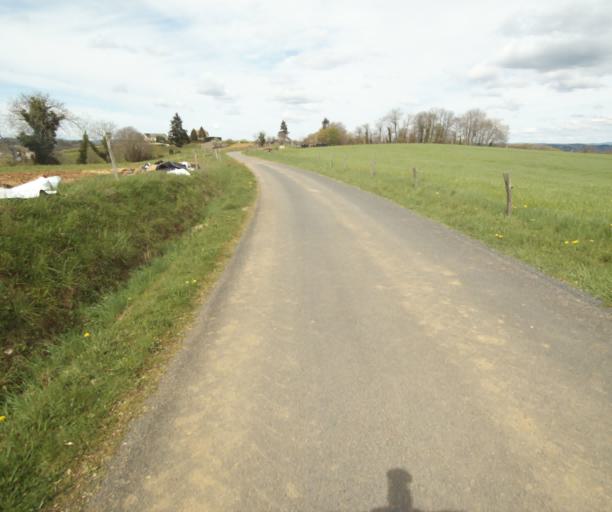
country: FR
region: Limousin
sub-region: Departement de la Correze
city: Laguenne
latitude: 45.2150
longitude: 1.8538
